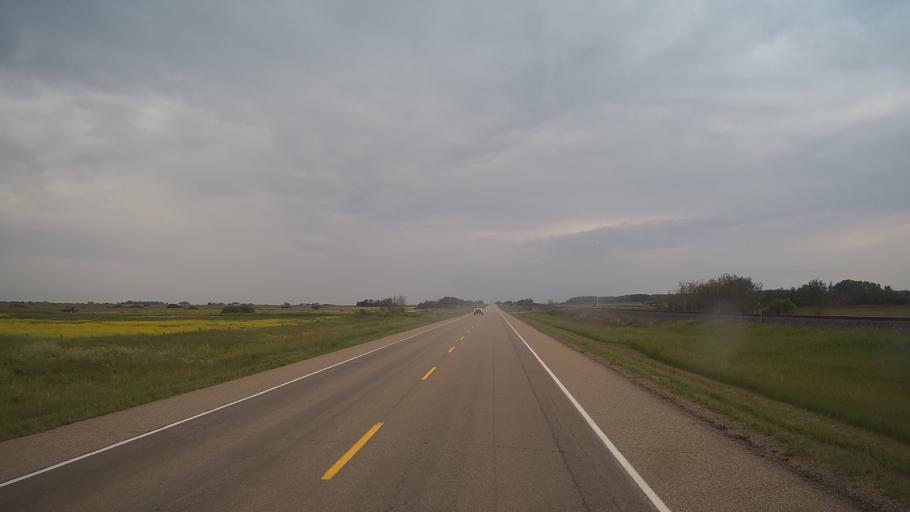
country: CA
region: Saskatchewan
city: Langham
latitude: 52.1272
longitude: -107.2613
